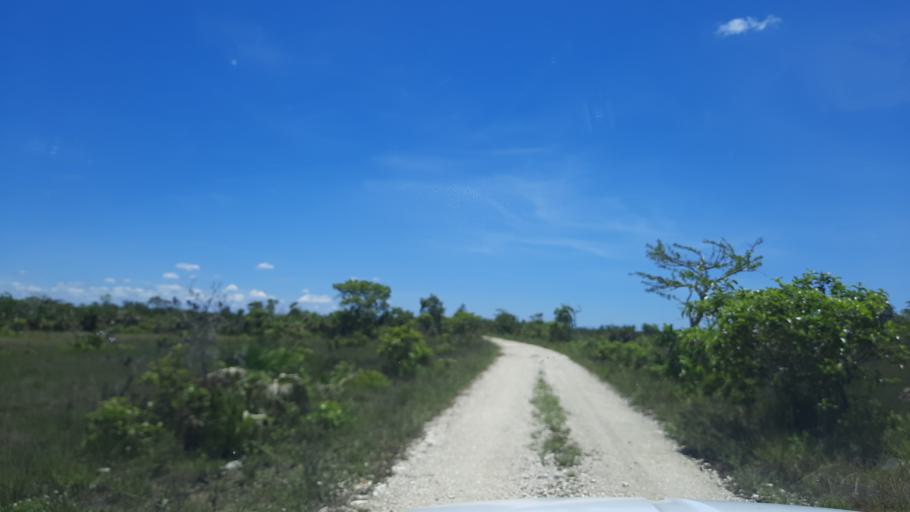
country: BZ
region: Cayo
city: Belmopan
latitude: 17.3815
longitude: -88.4969
